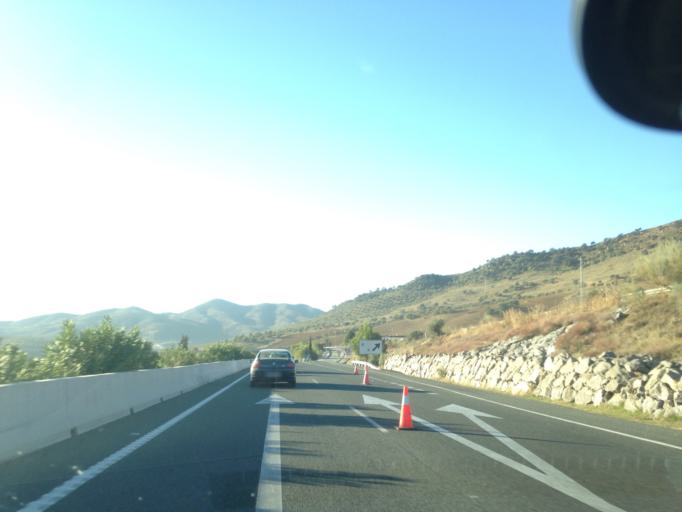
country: ES
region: Andalusia
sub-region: Provincia de Malaga
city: Casabermeja
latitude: 36.9275
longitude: -4.4469
